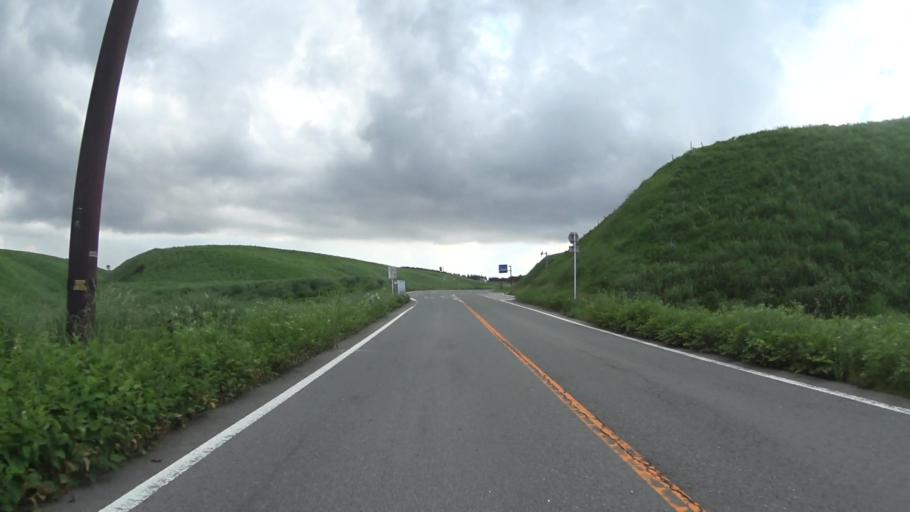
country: JP
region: Kumamoto
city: Aso
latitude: 33.0026
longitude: 131.1399
